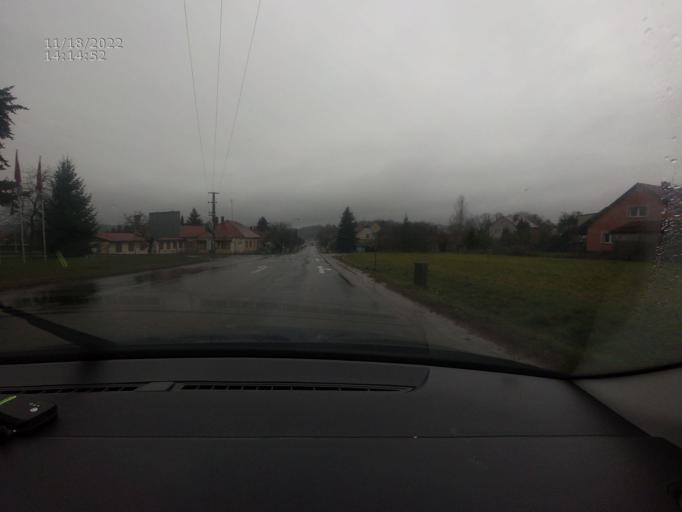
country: CZ
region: Jihocesky
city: Mirotice
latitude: 49.4239
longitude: 14.0362
